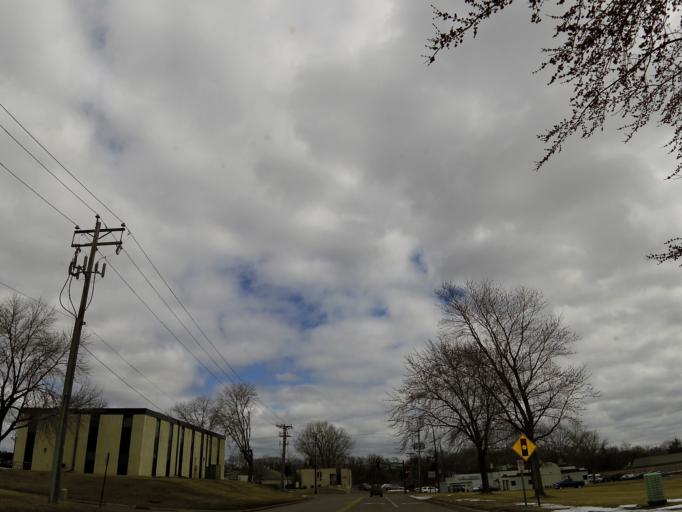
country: US
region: Minnesota
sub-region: Washington County
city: Woodbury
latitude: 44.9229
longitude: -92.9677
